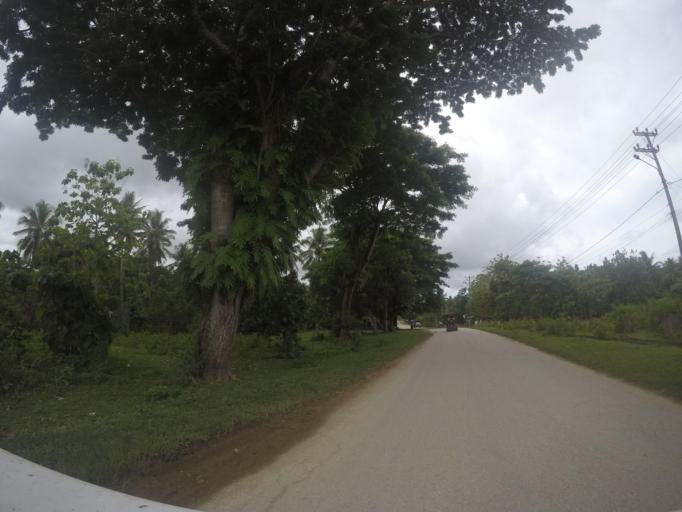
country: TL
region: Lautem
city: Lospalos
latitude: -8.5122
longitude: 126.9868
